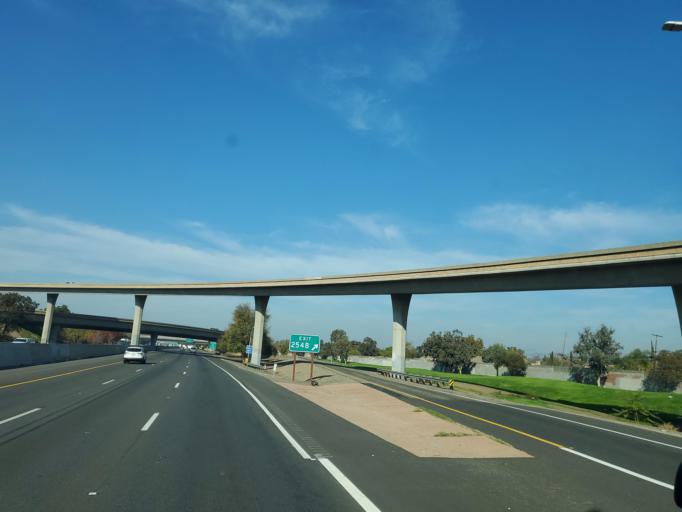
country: US
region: California
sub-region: San Joaquin County
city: Garden Acres
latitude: 37.9603
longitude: -121.2412
